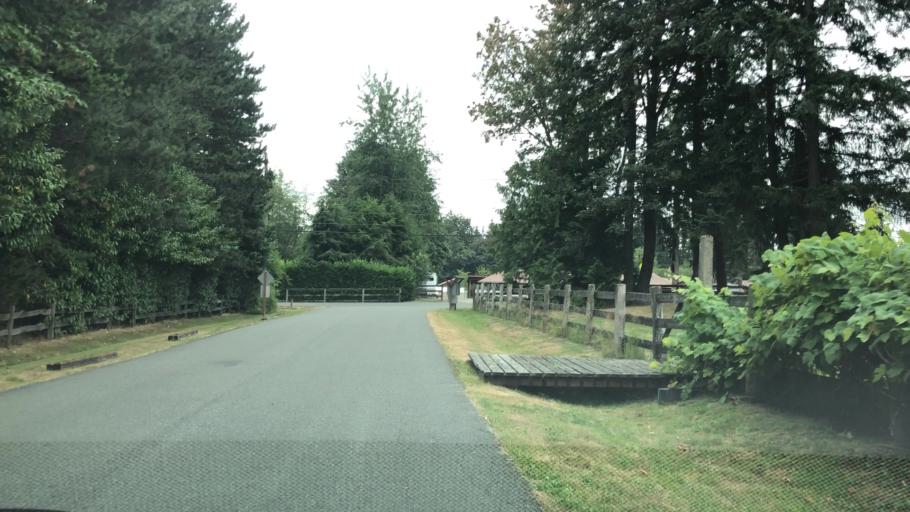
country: US
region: Washington
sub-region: King County
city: Cottage Lake
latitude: 47.7443
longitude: -122.1165
